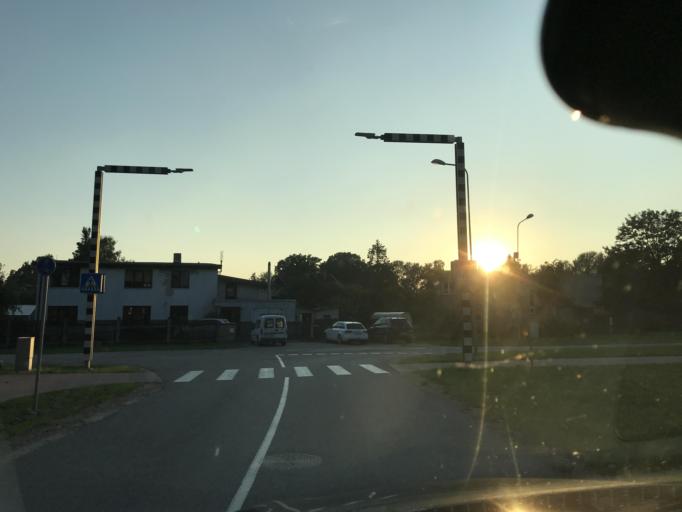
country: LV
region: Ikskile
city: Ikskile
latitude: 56.8316
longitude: 24.5042
